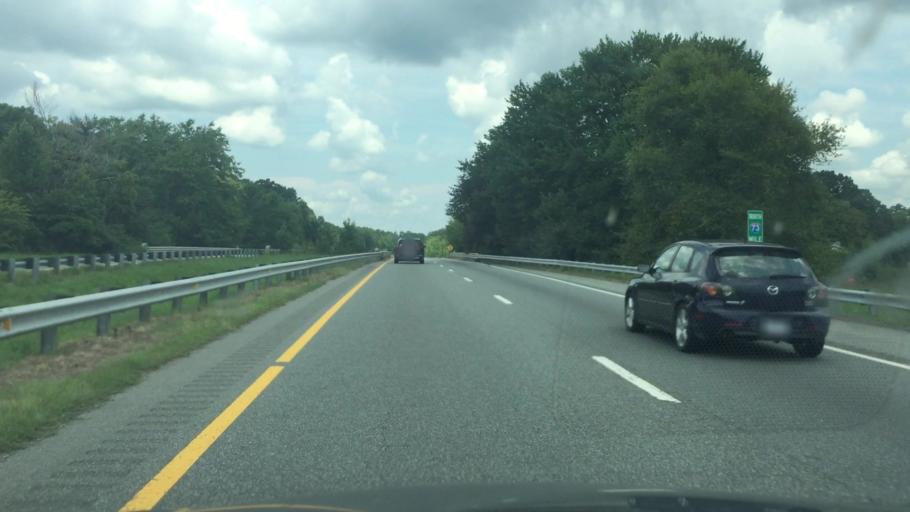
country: US
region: North Carolina
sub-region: Randolph County
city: Asheboro
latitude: 35.6197
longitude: -79.8251
